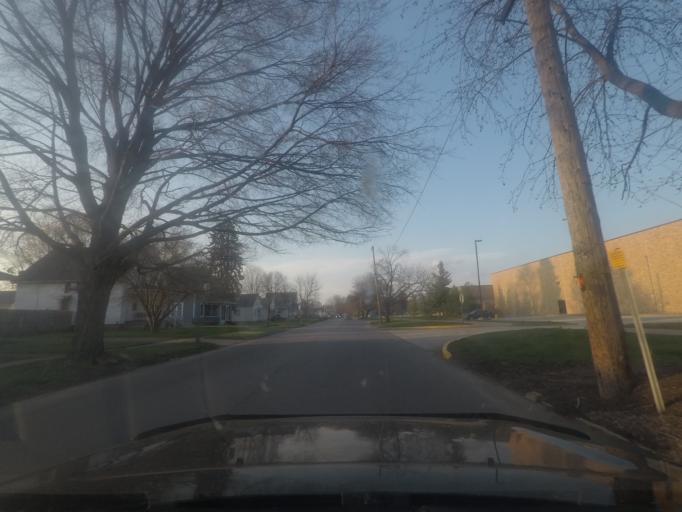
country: US
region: Indiana
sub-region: LaPorte County
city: LaPorte
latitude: 41.5997
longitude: -86.7292
